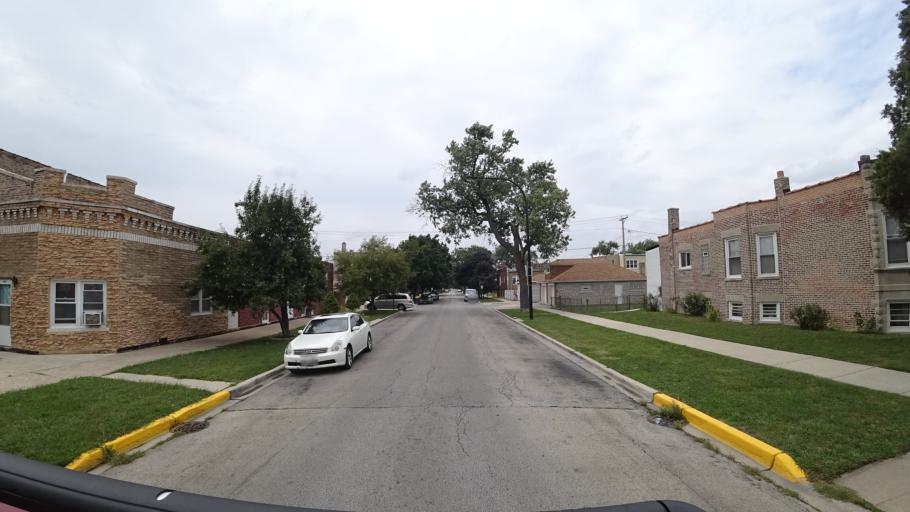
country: US
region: Illinois
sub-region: Cook County
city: Cicero
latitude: 41.8619
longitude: -87.7656
